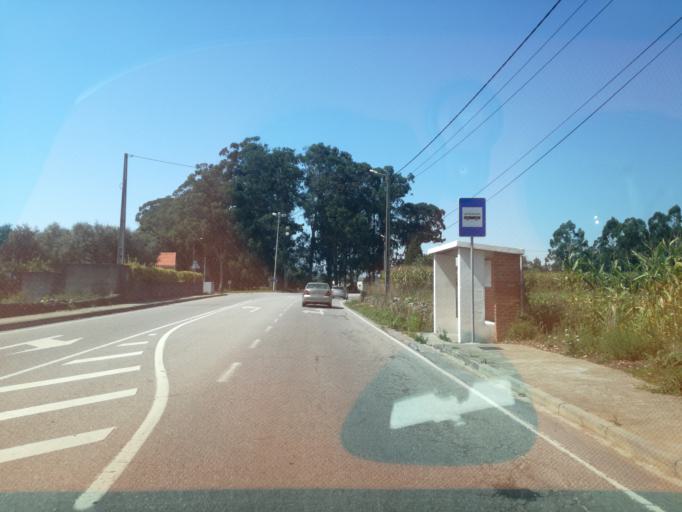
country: PT
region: Braga
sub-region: Esposende
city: Apulia
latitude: 41.4809
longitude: -8.7481
